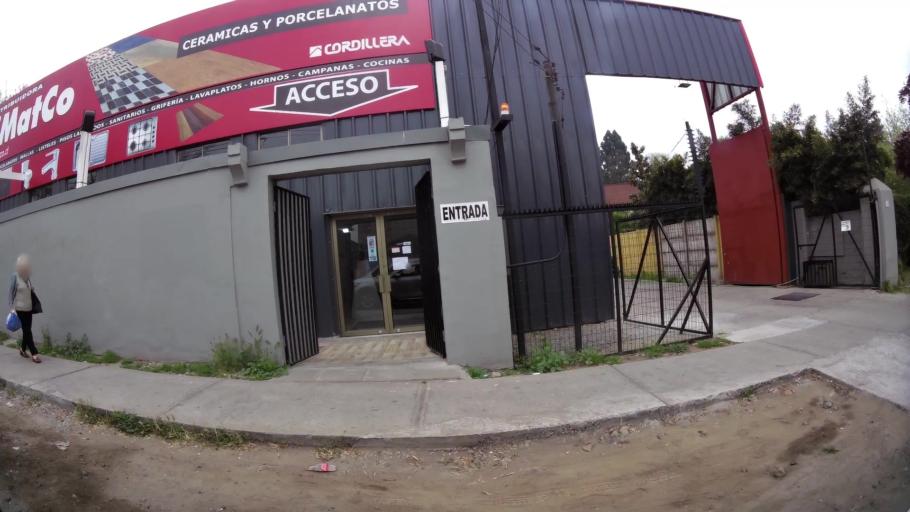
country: CL
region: Santiago Metropolitan
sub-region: Provincia de Santiago
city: Lo Prado
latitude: -33.5014
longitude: -70.7579
